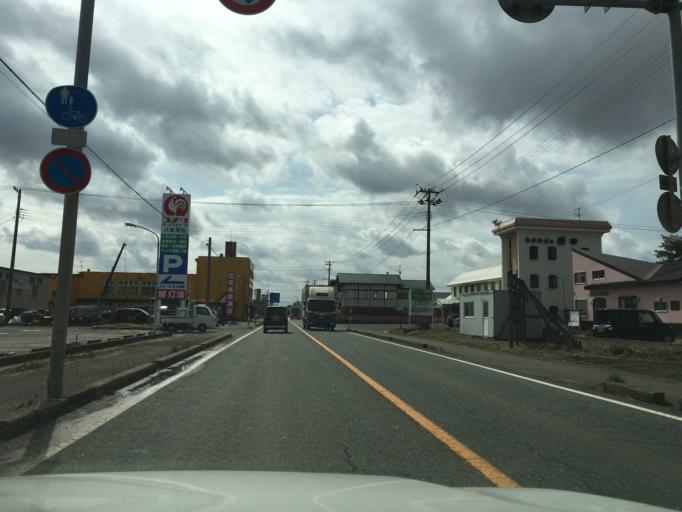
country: JP
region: Akita
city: Tenno
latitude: 39.9470
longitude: 140.0836
